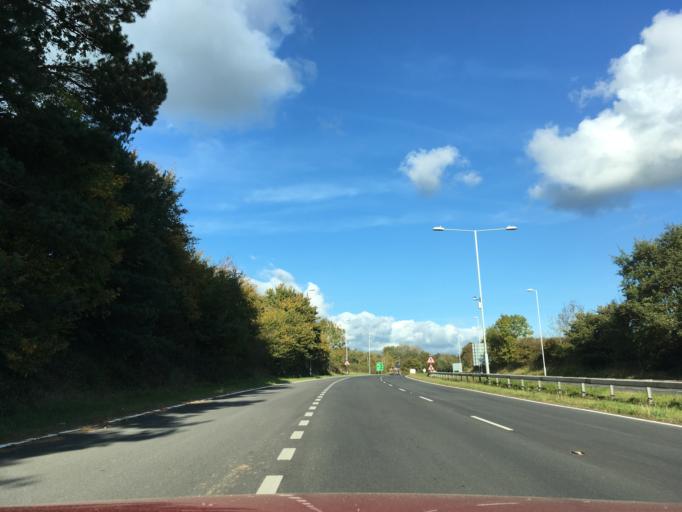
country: GB
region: Wales
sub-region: Sir Powys
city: Brecon
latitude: 51.9642
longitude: -3.3529
